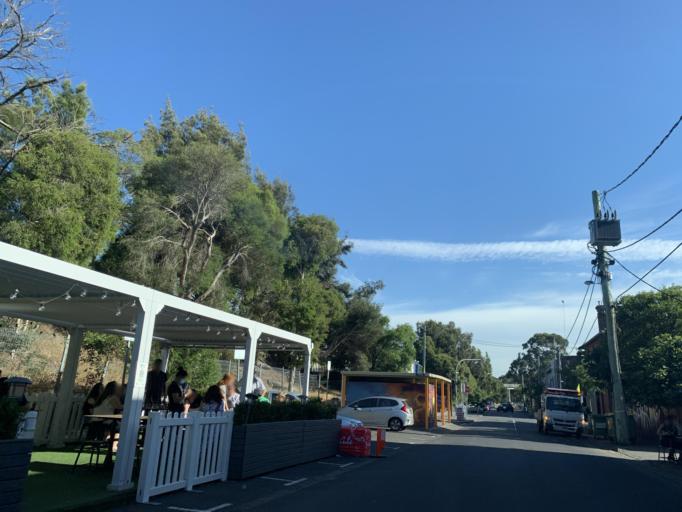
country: AU
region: Victoria
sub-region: Bayside
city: North Brighton
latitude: -37.8980
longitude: 145.0042
